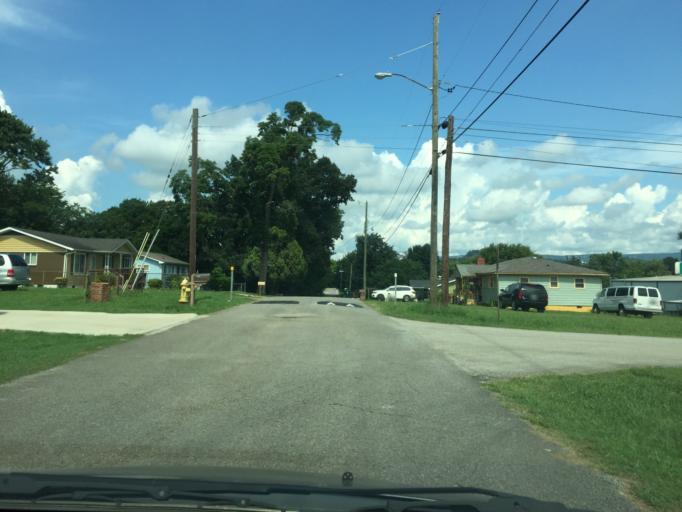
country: US
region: Tennessee
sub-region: Hamilton County
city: East Chattanooga
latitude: 35.0689
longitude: -85.2670
